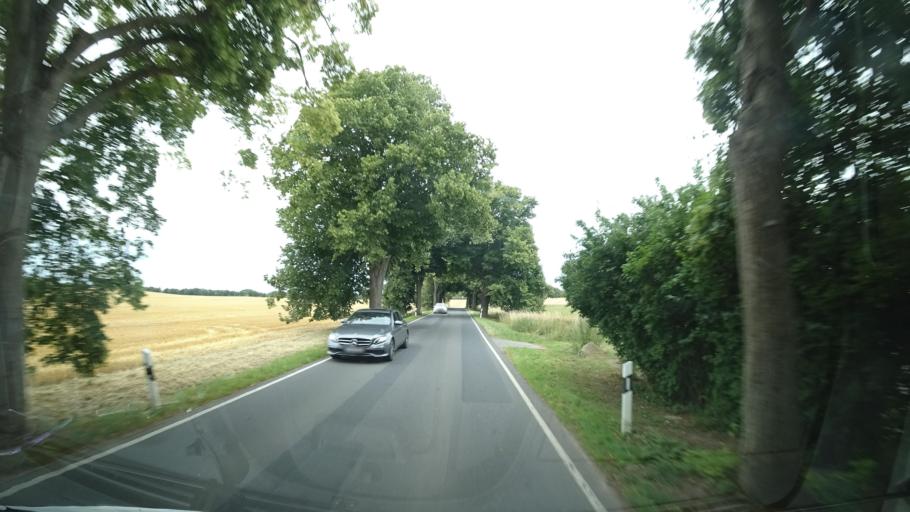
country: DE
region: Mecklenburg-Vorpommern
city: Poseritz
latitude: 54.3061
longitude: 13.2267
